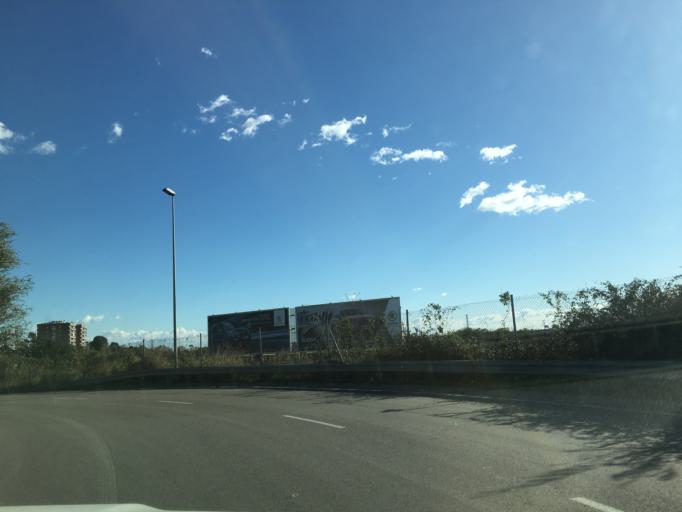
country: ES
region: Catalonia
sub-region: Provincia de Barcelona
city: Sant Joan Despi
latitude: 41.3610
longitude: 2.0555
